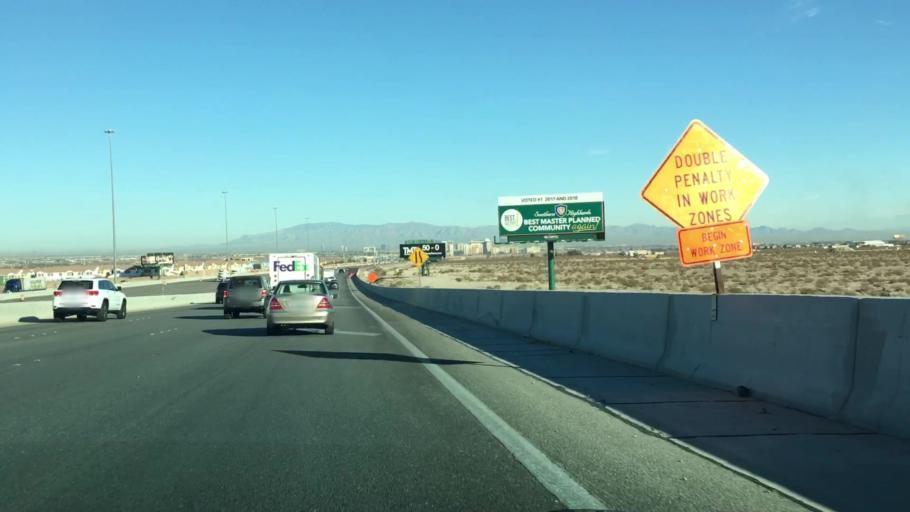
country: US
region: Nevada
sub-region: Clark County
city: Enterprise
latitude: 35.9650
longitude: -115.1808
